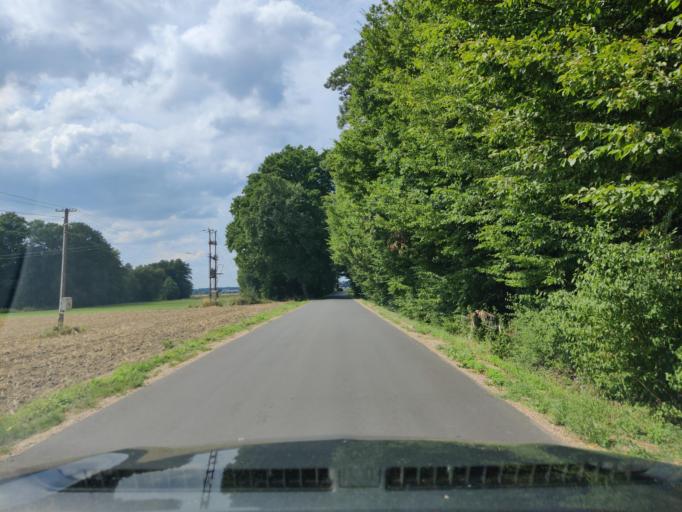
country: PL
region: Masovian Voivodeship
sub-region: Powiat pultuski
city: Obryte
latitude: 52.6912
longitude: 21.2135
